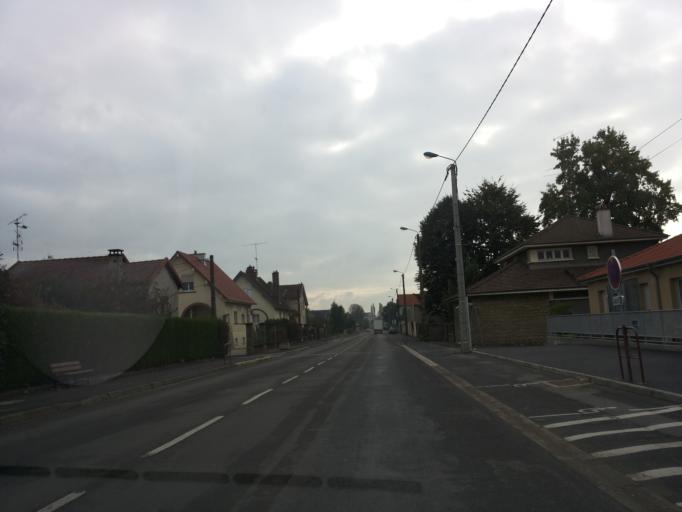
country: FR
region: Champagne-Ardenne
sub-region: Departement des Ardennes
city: Blagny
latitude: 49.6233
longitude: 5.1833
